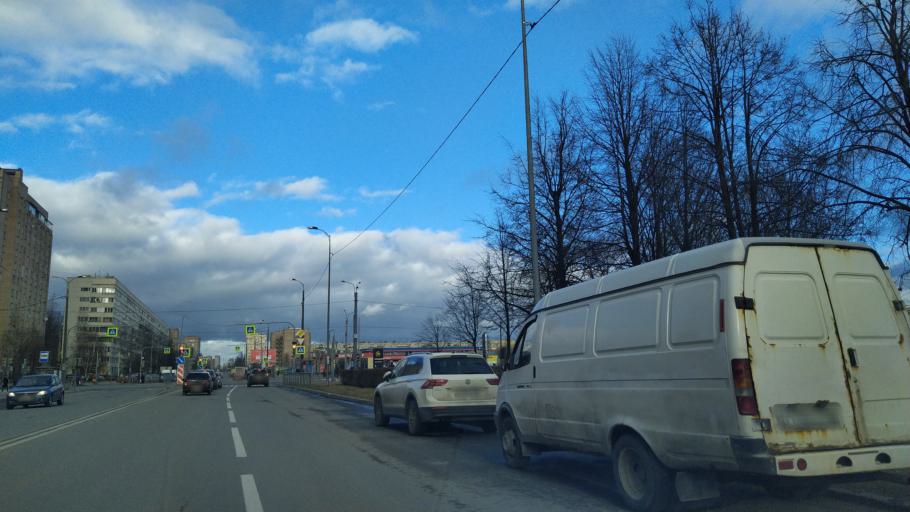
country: RU
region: St.-Petersburg
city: Grazhdanka
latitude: 60.0414
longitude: 30.3858
